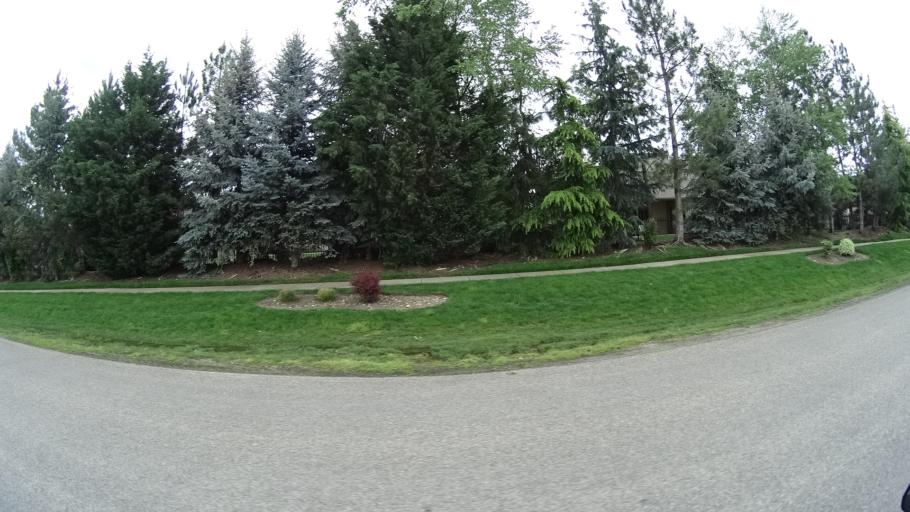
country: US
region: Idaho
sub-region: Ada County
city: Eagle
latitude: 43.6857
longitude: -116.3647
